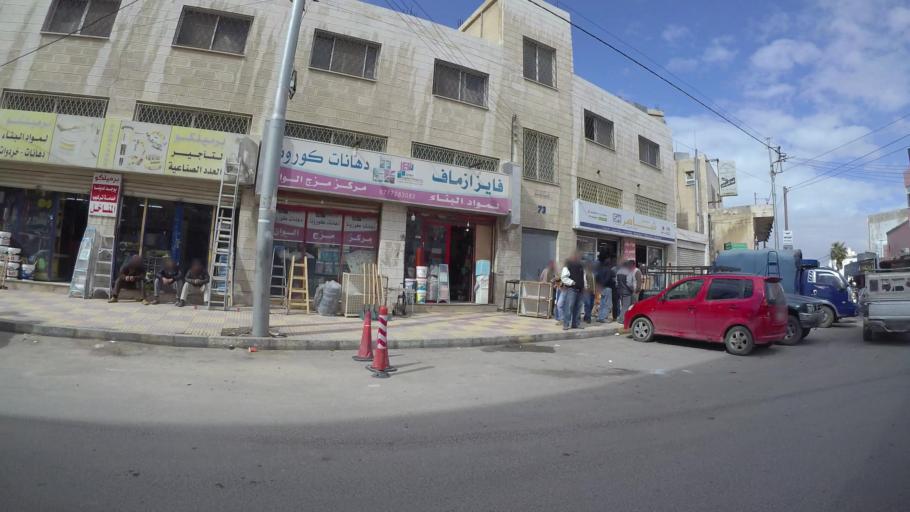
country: JO
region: Amman
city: Wadi as Sir
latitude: 31.9536
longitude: 35.8337
